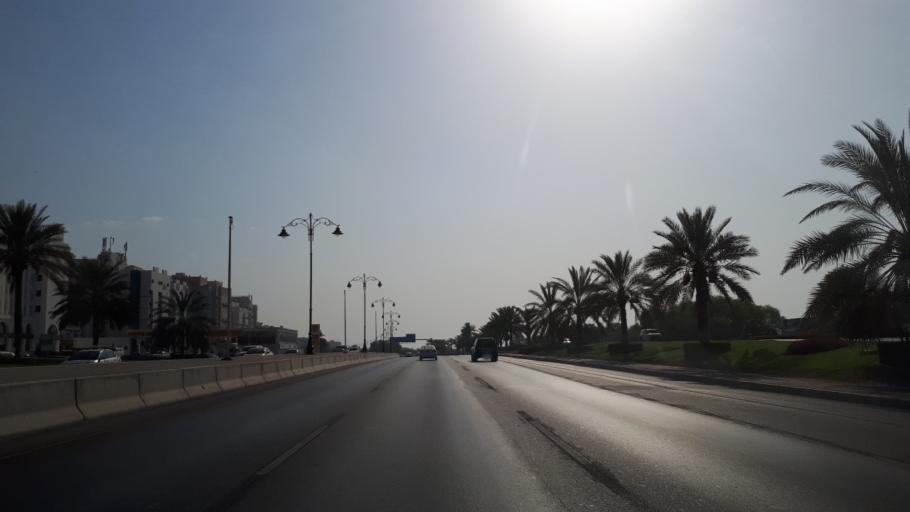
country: OM
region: Muhafazat Masqat
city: Bawshar
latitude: 23.5972
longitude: 58.4207
